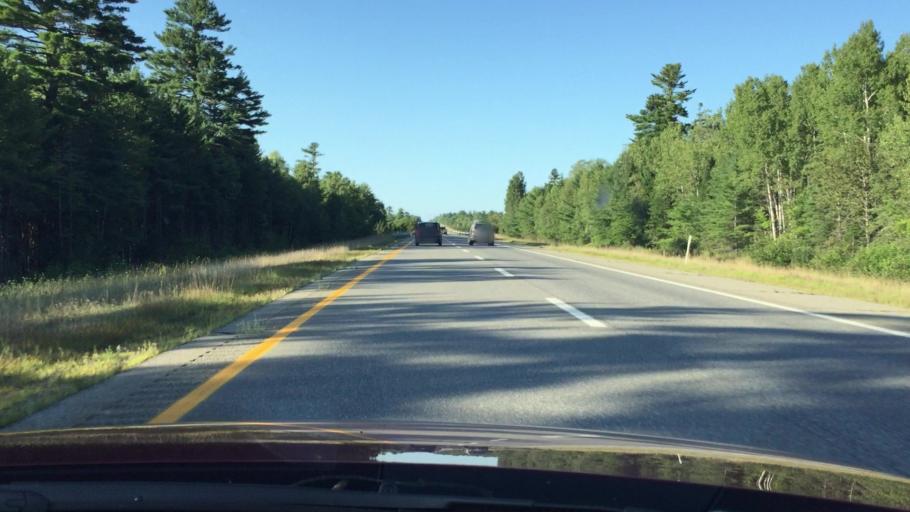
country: US
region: Maine
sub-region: Penobscot County
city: Lincoln
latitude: 45.3894
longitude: -68.6028
